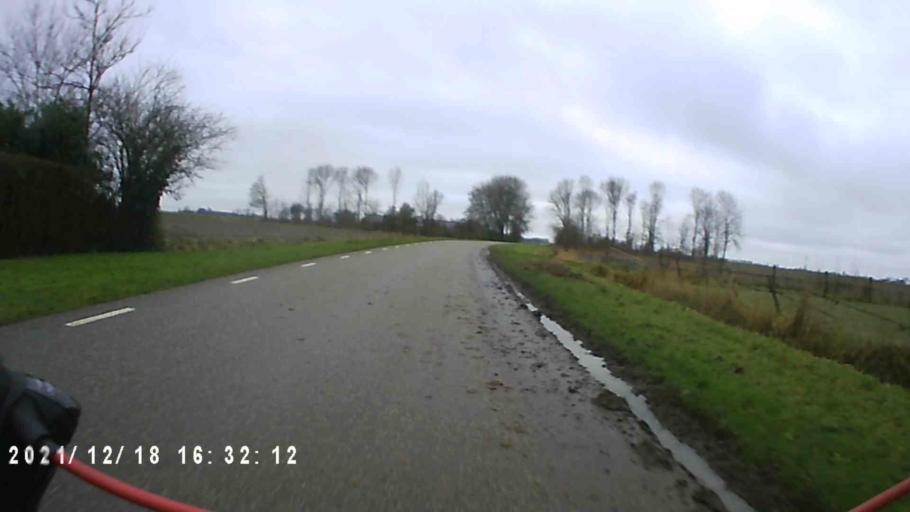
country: NL
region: Friesland
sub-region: Gemeente Dongeradeel
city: Dokkum
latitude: 53.3556
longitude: 6.0356
